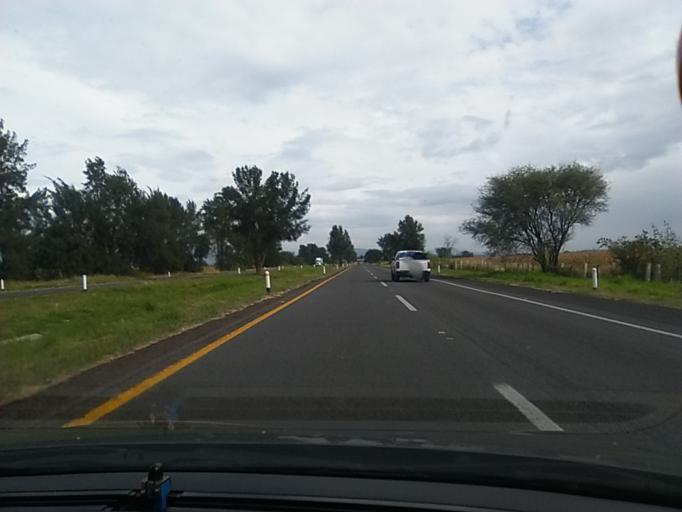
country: MX
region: Michoacan
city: Vistahermosa de Negrete
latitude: 20.3003
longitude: -102.4829
